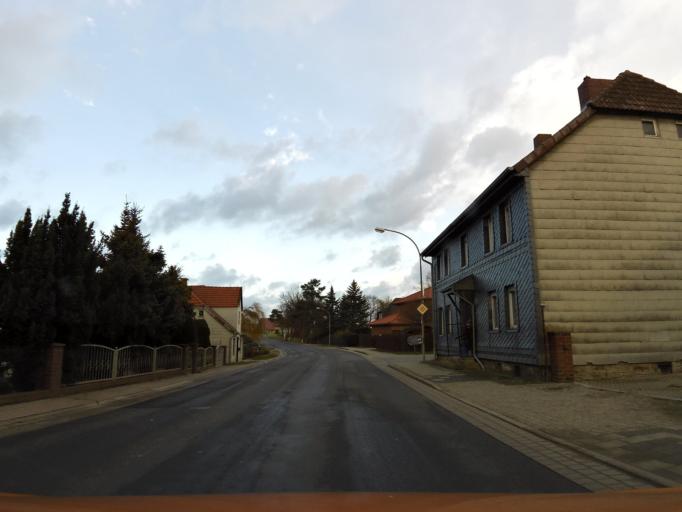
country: DE
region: Lower Saxony
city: Gross Twulpstedt
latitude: 52.3747
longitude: 10.9203
